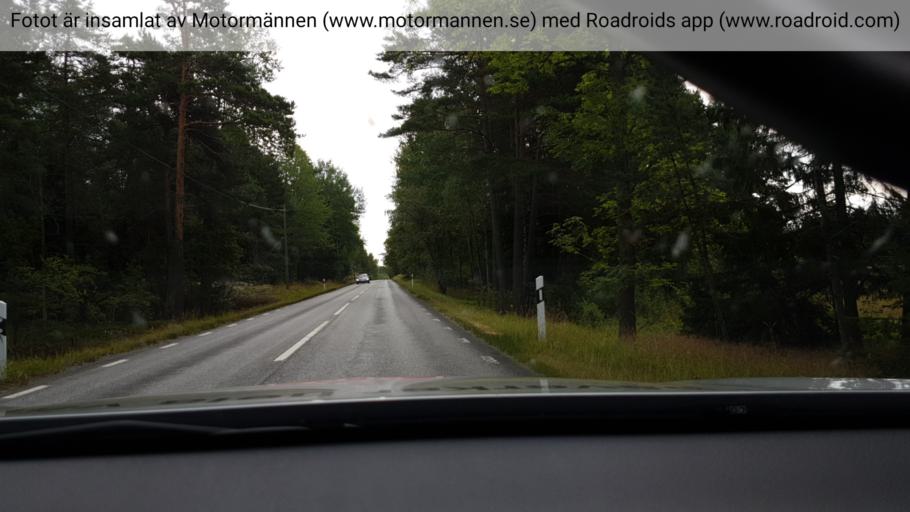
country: SE
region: Stockholm
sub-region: Vaxholms Kommun
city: Resaro
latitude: 59.5491
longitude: 18.4928
